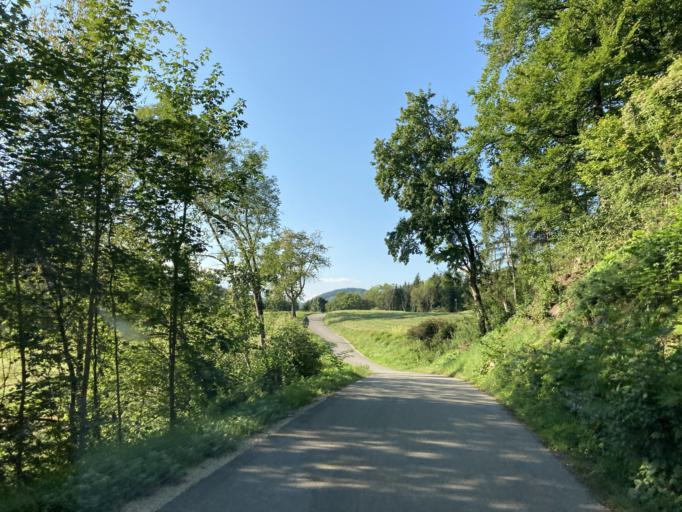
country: DE
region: Baden-Wuerttemberg
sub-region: Freiburg Region
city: Blumberg
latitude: 47.8264
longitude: 8.5094
